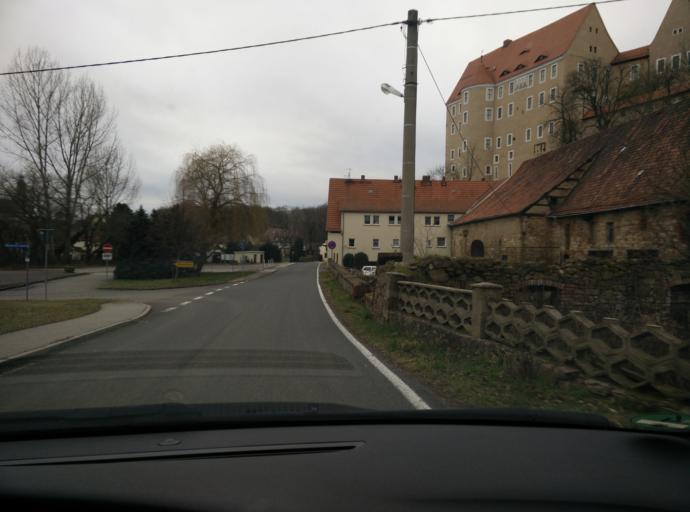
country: DE
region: Saxony
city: Frohburg
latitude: 51.0178
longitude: 12.5775
